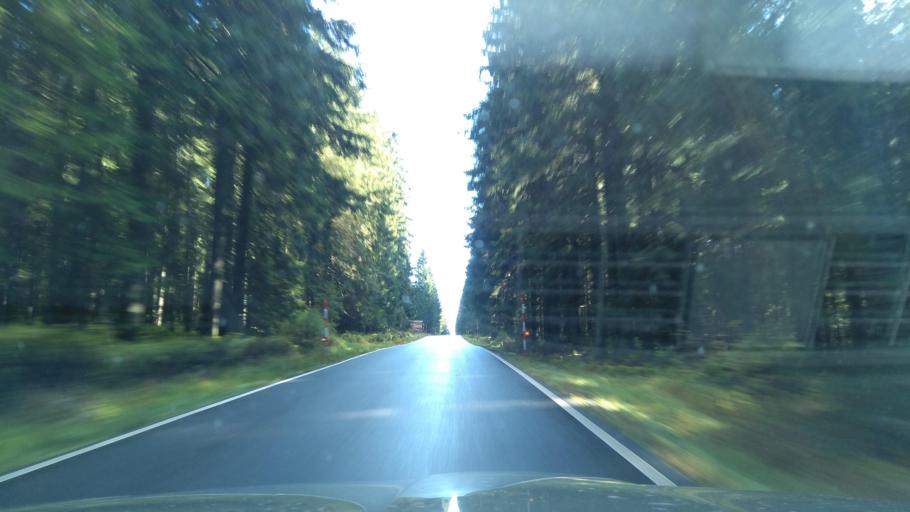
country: CZ
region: Plzensky
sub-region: Okres Klatovy
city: Kasperske Hory
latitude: 49.0276
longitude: 13.5368
